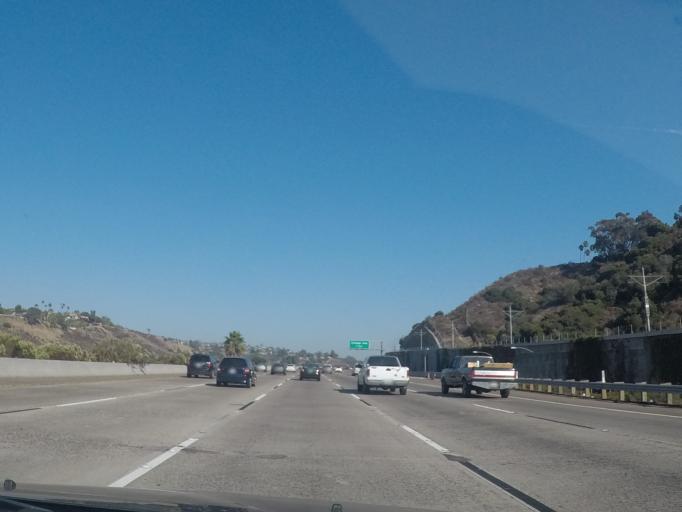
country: US
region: California
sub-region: San Diego County
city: La Mesa
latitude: 32.7806
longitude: -117.0891
